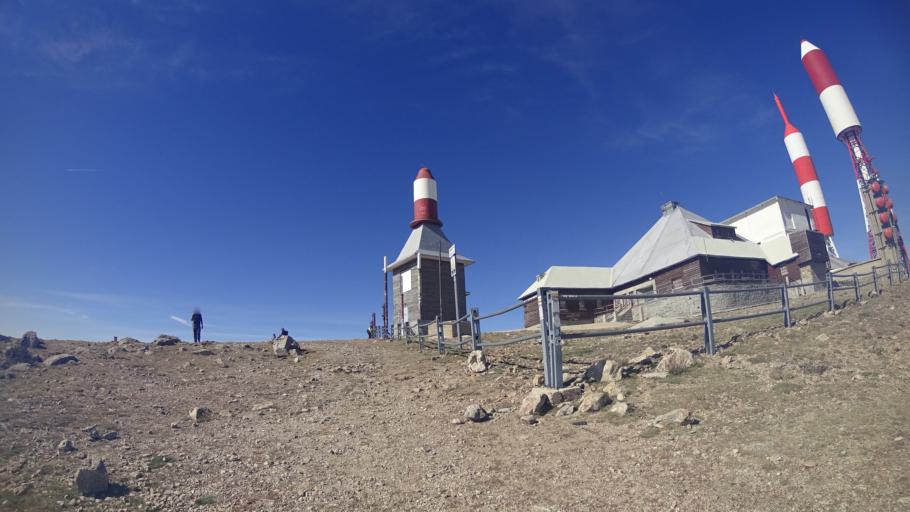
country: ES
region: Madrid
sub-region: Provincia de Madrid
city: Navacerrada
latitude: 40.7842
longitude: -3.9793
